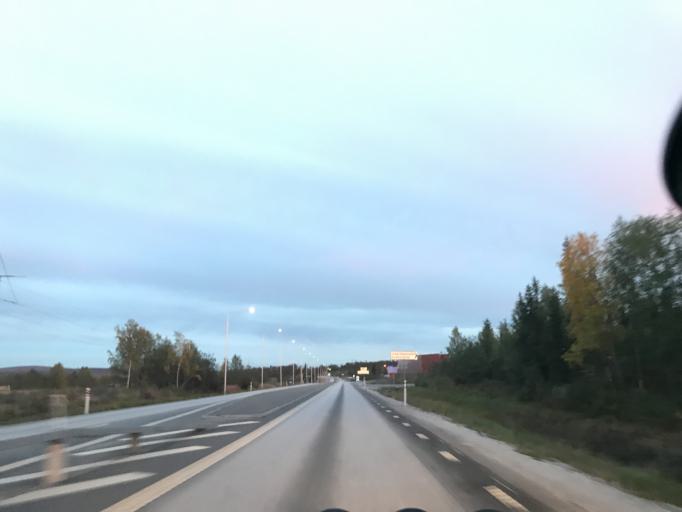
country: SE
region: Norrbotten
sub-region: Gallivare Kommun
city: Malmberget
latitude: 67.6549
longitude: 21.0126
